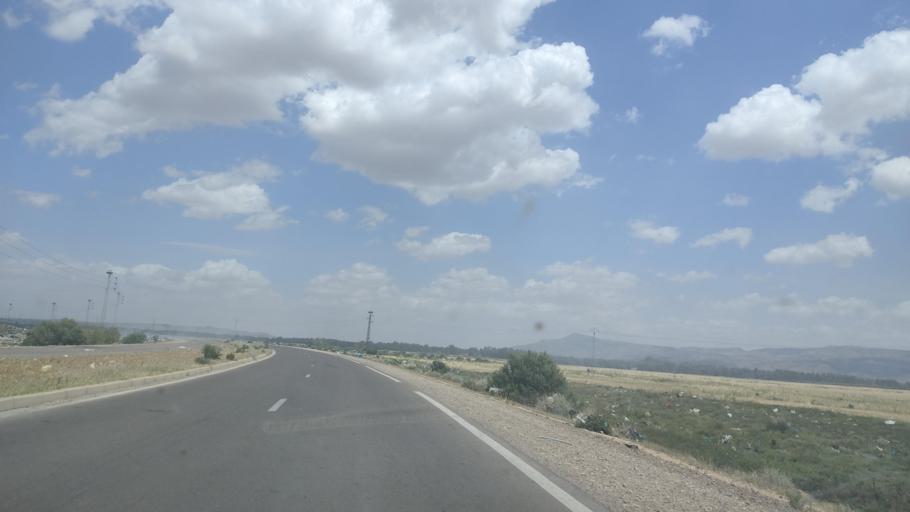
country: TN
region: Al Qasrayn
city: Kasserine
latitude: 35.1977
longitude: 8.8492
